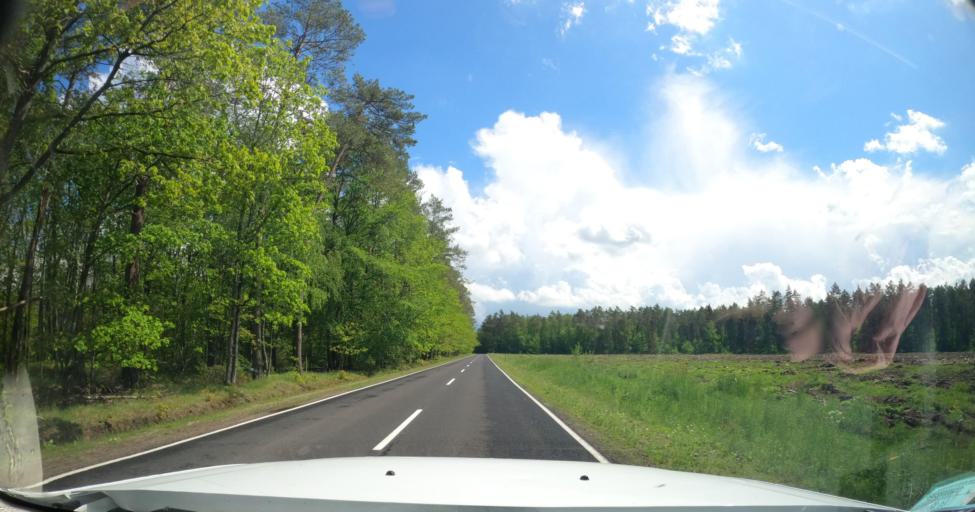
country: PL
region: Pomeranian Voivodeship
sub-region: Powiat bytowski
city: Czarna Dabrowka
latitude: 54.3865
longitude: 17.4803
